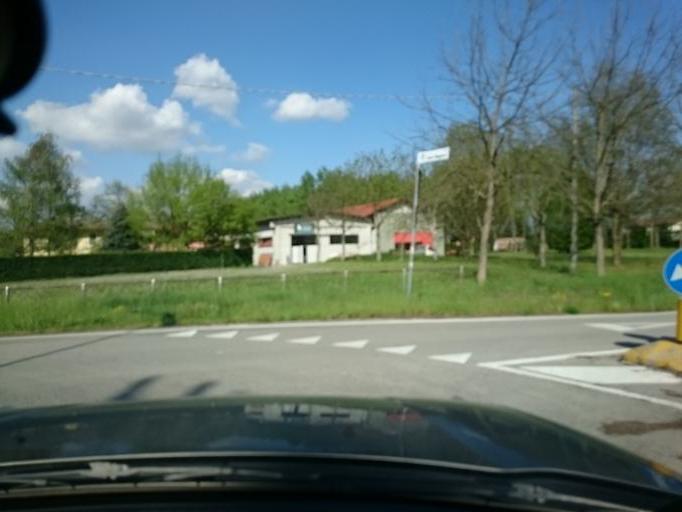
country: IT
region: Veneto
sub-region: Provincia di Padova
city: Pionca
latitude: 45.4688
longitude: 11.9792
